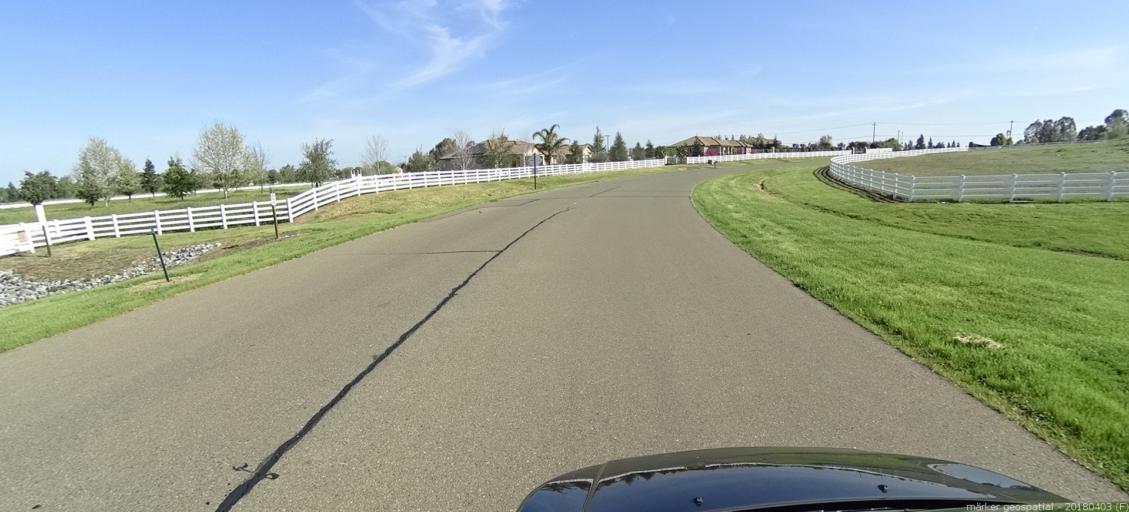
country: US
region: California
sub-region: Sacramento County
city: Wilton
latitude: 38.4220
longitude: -121.1959
